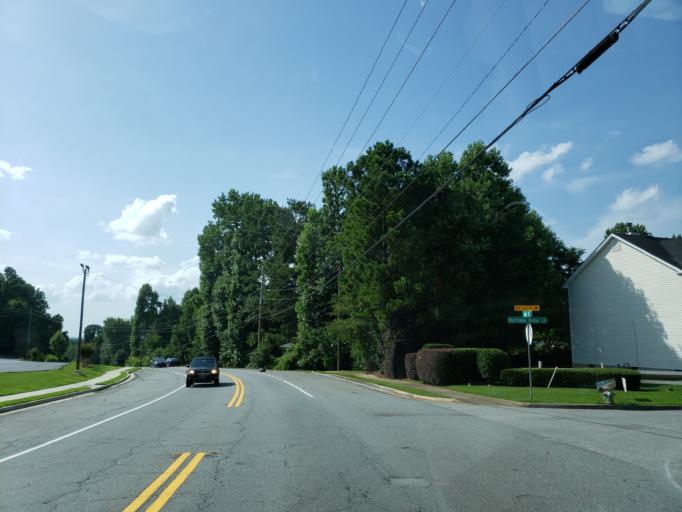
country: US
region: Georgia
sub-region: Cobb County
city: Mableton
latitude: 33.8642
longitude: -84.5990
